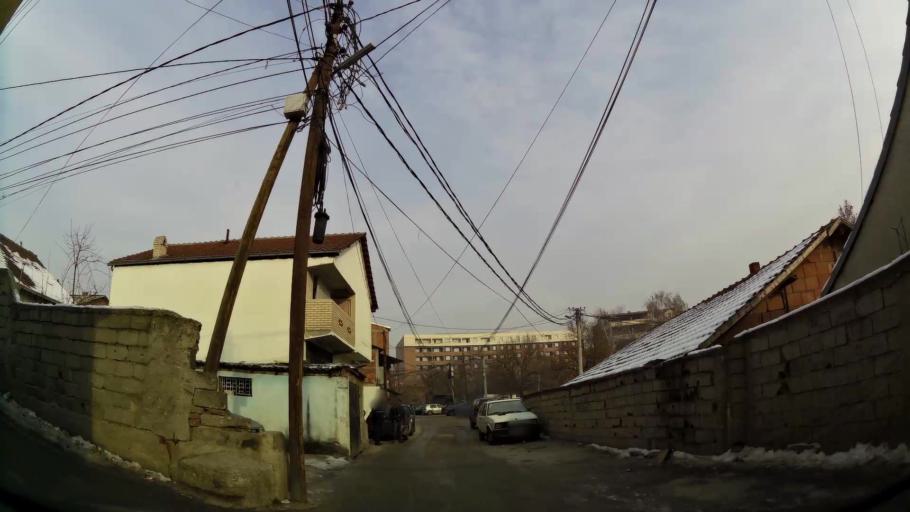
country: MK
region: Cair
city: Cair
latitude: 42.0202
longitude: 21.4387
